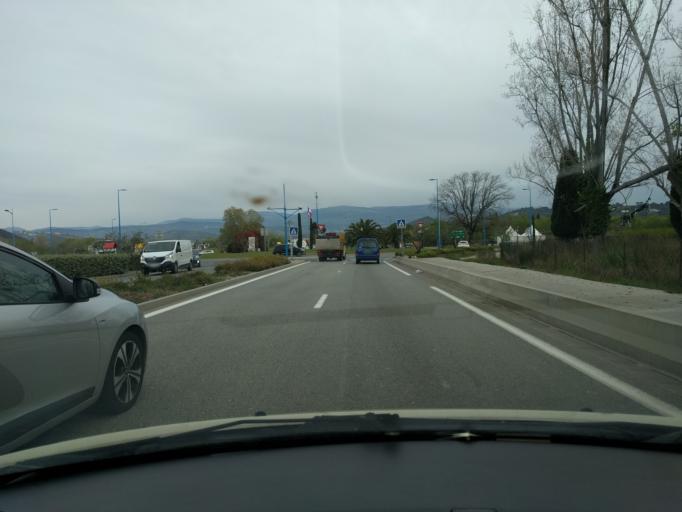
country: FR
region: Provence-Alpes-Cote d'Azur
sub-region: Departement des Alpes-Maritimes
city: Mandelieu-la-Napoule
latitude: 43.5661
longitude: 6.9490
